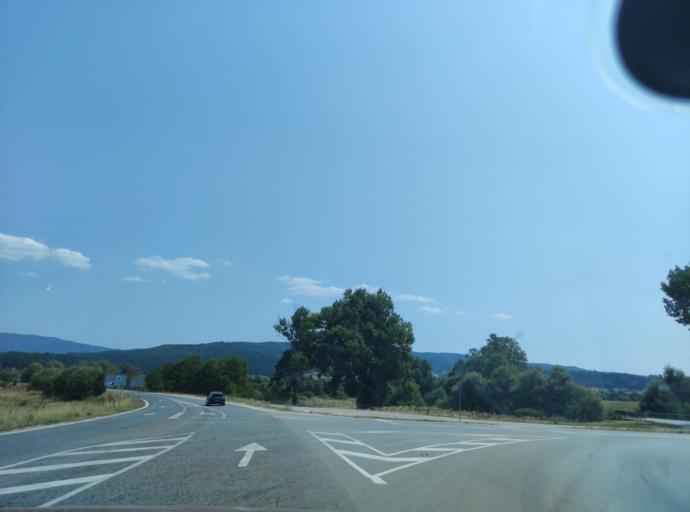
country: BG
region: Blagoevgrad
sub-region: Obshtina Razlog
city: Razlog
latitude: 41.8865
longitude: 23.5079
